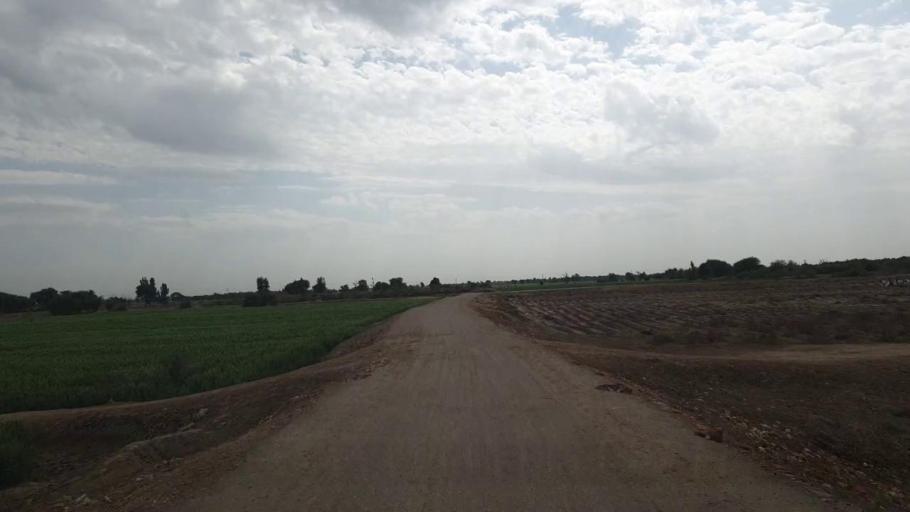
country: PK
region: Sindh
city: Hala
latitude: 25.9267
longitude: 68.4337
